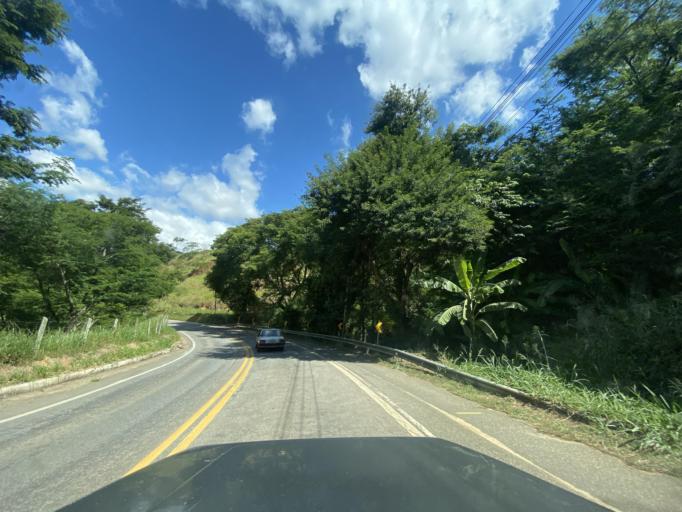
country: BR
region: Espirito Santo
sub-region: Alegre
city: Alegre
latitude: -20.7580
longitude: -41.5011
